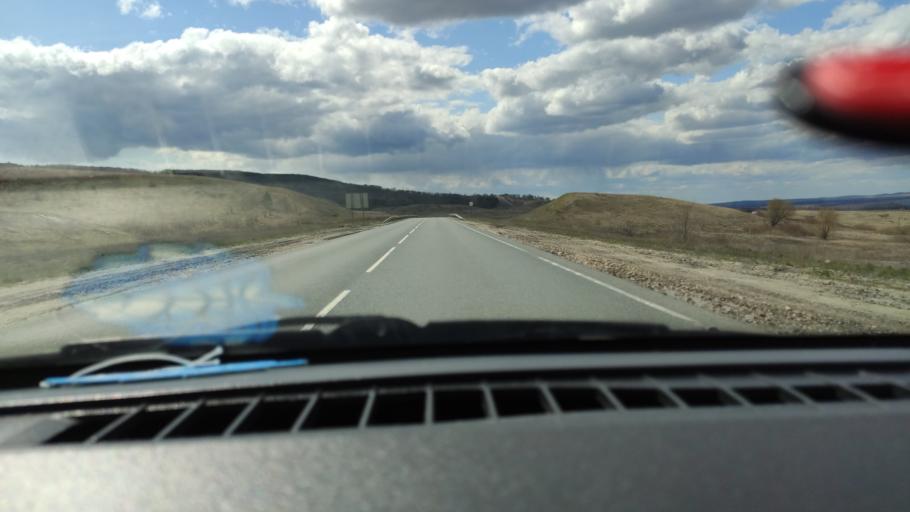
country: RU
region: Saratov
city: Alekseyevka
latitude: 52.3378
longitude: 47.9324
